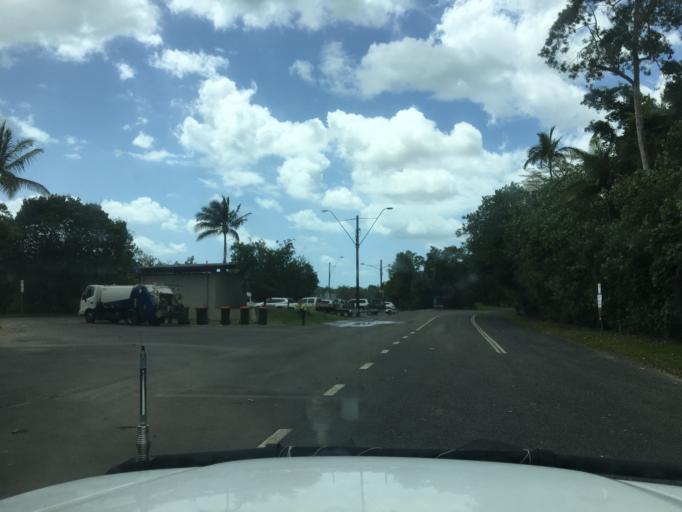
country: AU
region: Queensland
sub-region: Cairns
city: Woree
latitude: -17.2170
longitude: 145.9196
